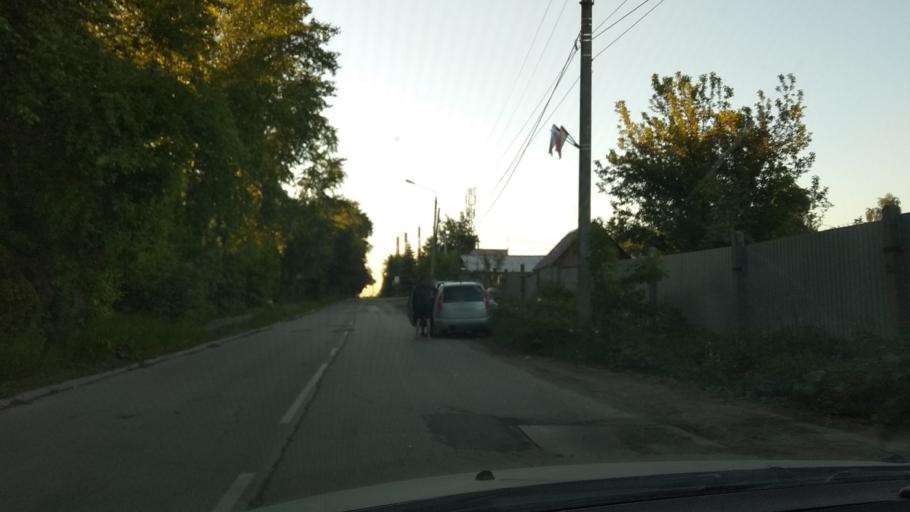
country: RU
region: Sverdlovsk
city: Sredneuralsk
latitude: 56.9858
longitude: 60.4599
